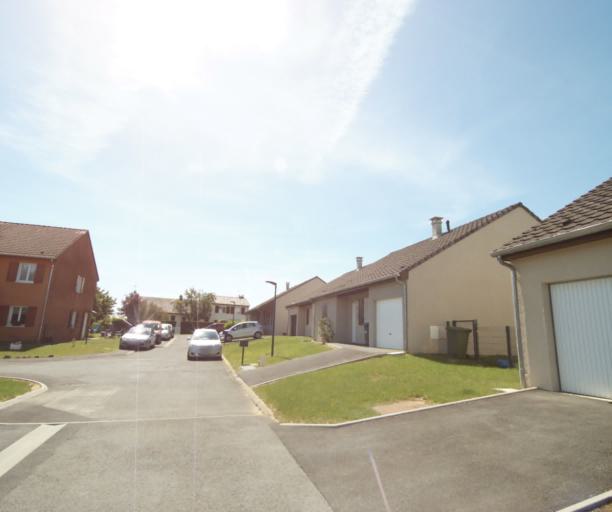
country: FR
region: Champagne-Ardenne
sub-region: Departement des Ardennes
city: La Francheville
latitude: 49.7461
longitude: 4.7116
